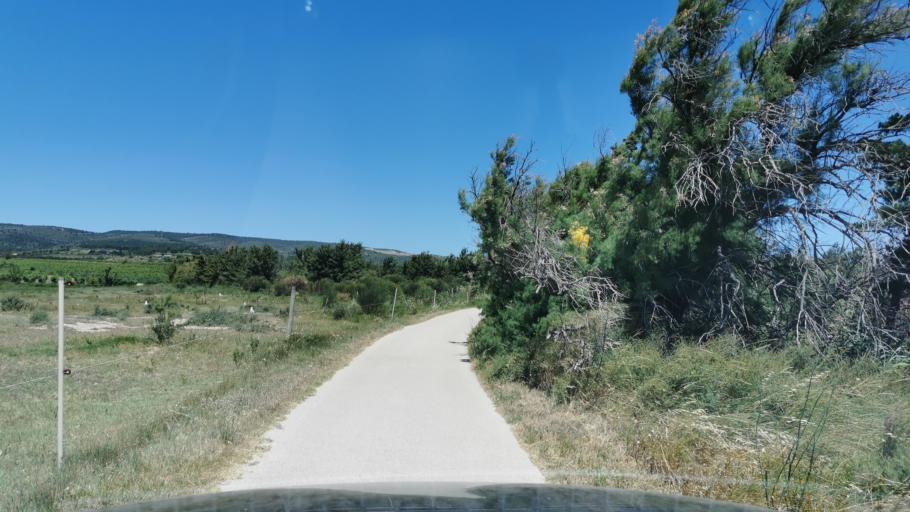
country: FR
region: Languedoc-Roussillon
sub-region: Departement de l'Aude
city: Peyriac-de-Mer
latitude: 43.1020
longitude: 2.9594
